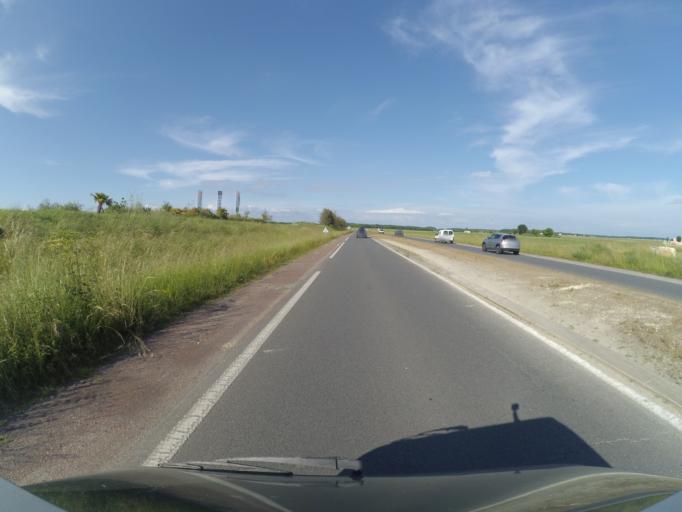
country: FR
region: Poitou-Charentes
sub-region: Departement de la Charente-Maritime
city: Saint-Sulpice-de-Royan
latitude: 45.6661
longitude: -1.0110
